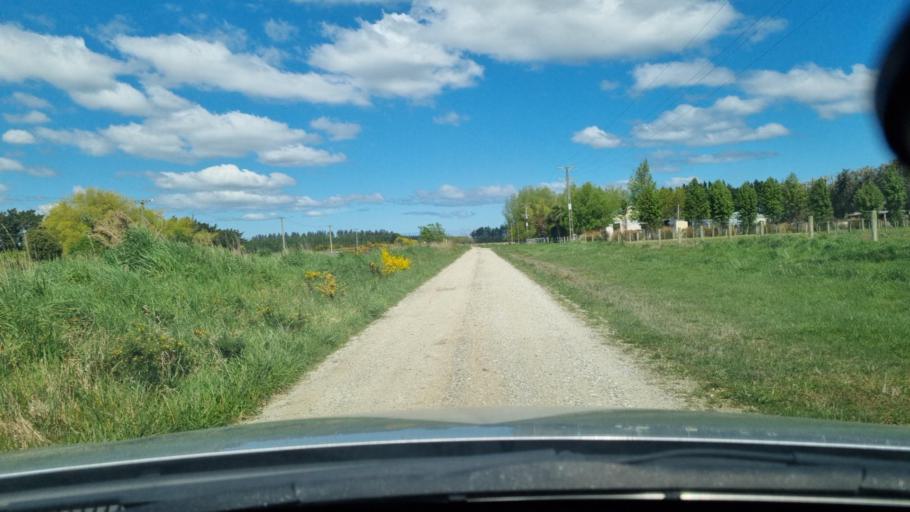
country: NZ
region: Southland
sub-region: Invercargill City
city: Invercargill
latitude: -46.3473
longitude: 168.3400
